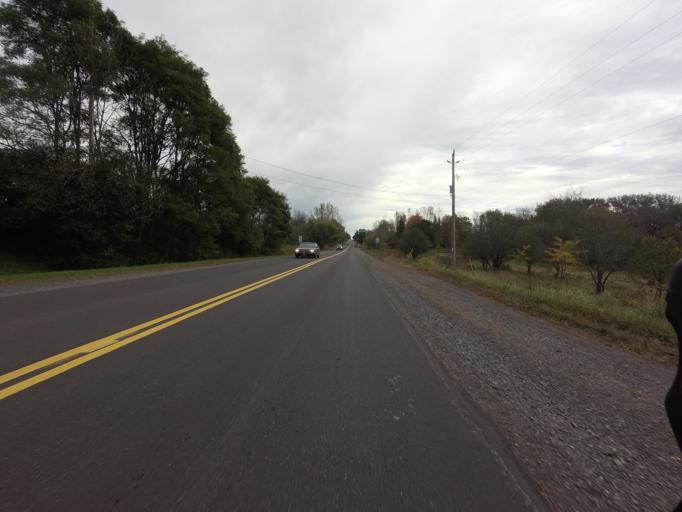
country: CA
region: Ontario
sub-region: Lanark County
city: Smiths Falls
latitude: 44.9819
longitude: -75.8055
